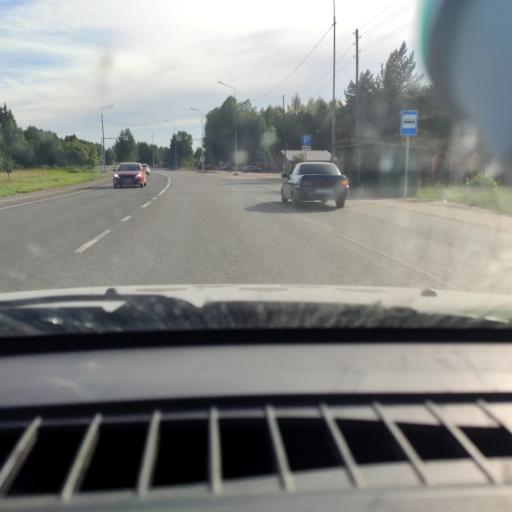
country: RU
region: Kirov
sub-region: Kirovo-Chepetskiy Rayon
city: Kirov
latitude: 58.6213
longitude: 49.7767
